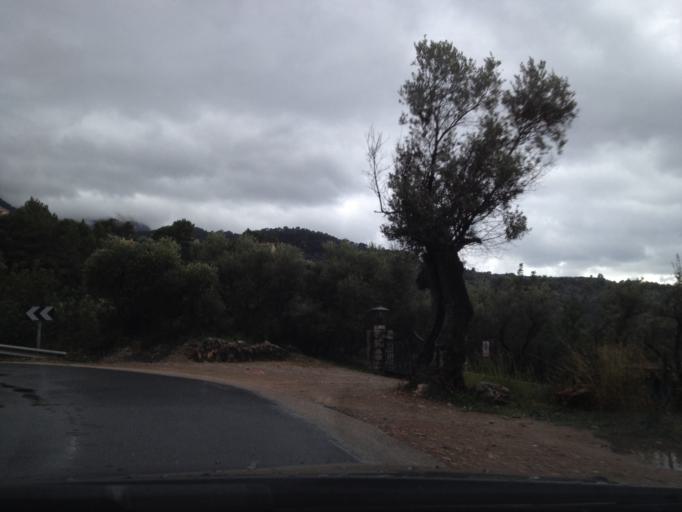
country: ES
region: Balearic Islands
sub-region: Illes Balears
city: Deia
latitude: 39.7590
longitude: 2.6502
